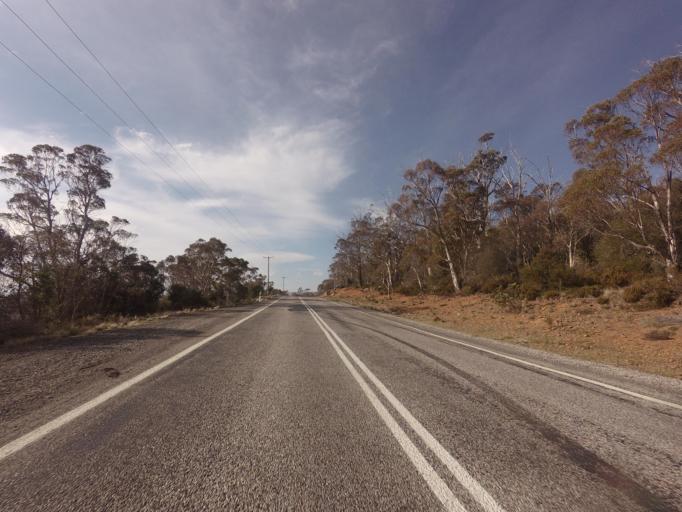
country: AU
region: Tasmania
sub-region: Meander Valley
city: Deloraine
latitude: -41.9855
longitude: 146.7126
